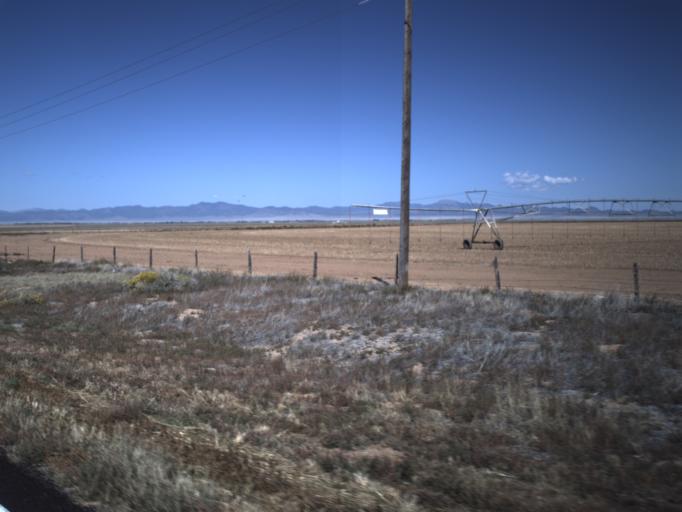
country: US
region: Utah
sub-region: Washington County
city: Enterprise
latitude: 37.6779
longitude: -113.5684
